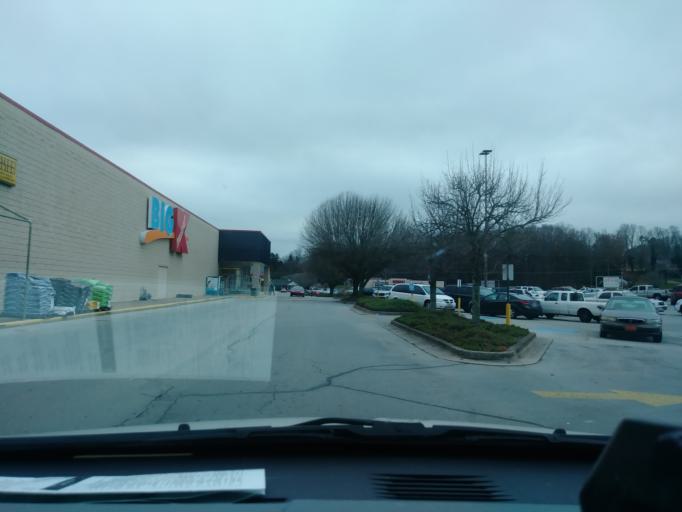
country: US
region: Tennessee
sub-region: Greene County
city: Greeneville
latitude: 36.1753
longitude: -82.7964
